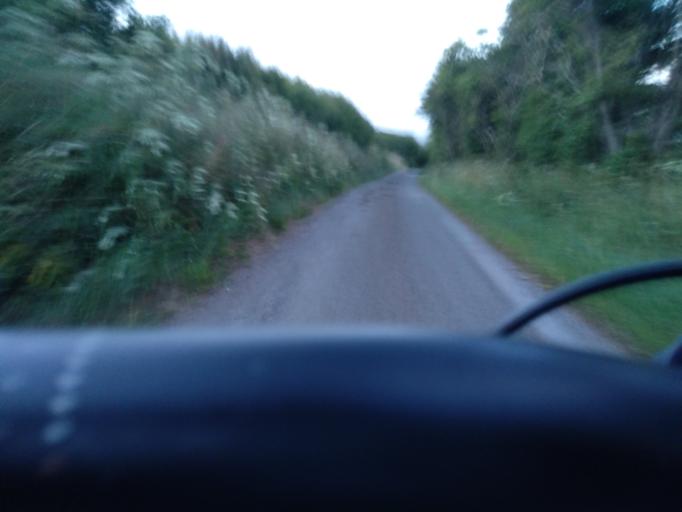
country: GB
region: England
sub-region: Isle of Wight
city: Ventnor
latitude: 50.6075
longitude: -1.2388
